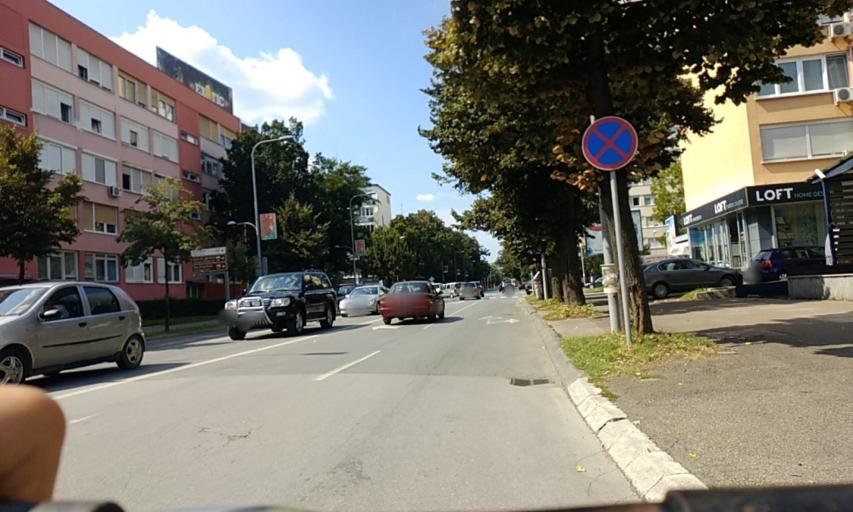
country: BA
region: Republika Srpska
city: Mejdan - Obilicevo
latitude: 44.7687
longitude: 17.1874
